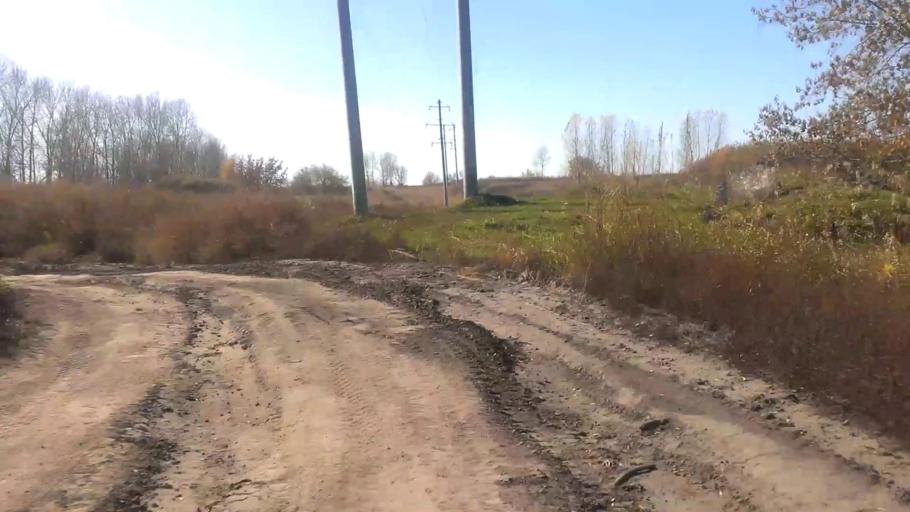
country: RU
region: Altai Krai
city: Novoaltaysk
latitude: 53.3689
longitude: 83.9490
